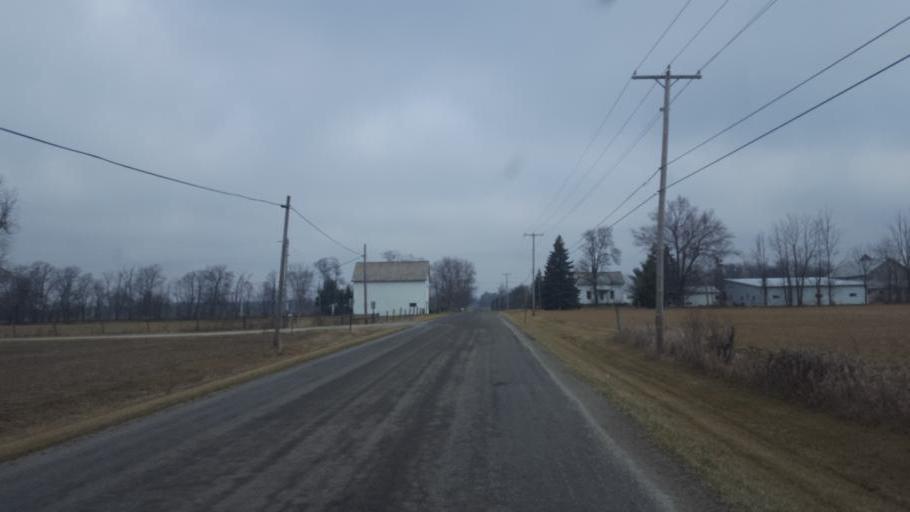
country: US
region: Ohio
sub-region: Morrow County
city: Mount Gilead
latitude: 40.5777
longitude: -82.8619
